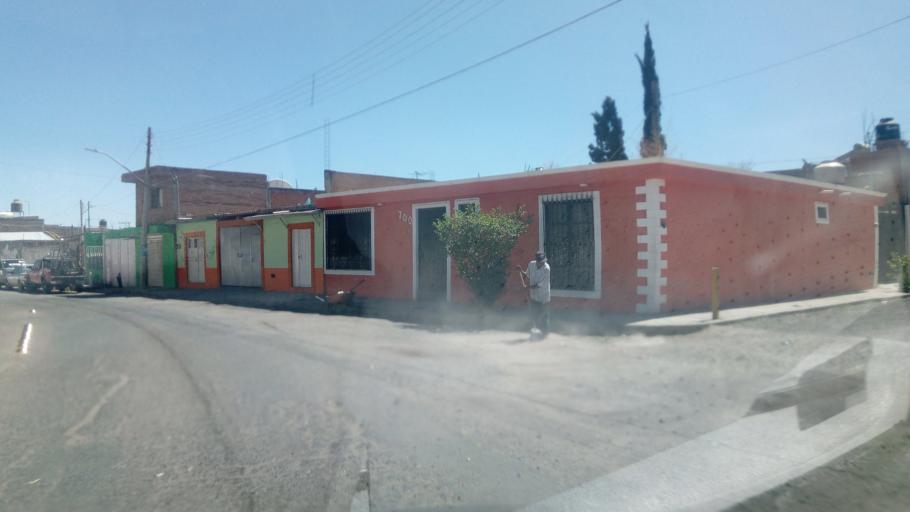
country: MX
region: Durango
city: Victoria de Durango
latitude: 24.0146
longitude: -104.6573
